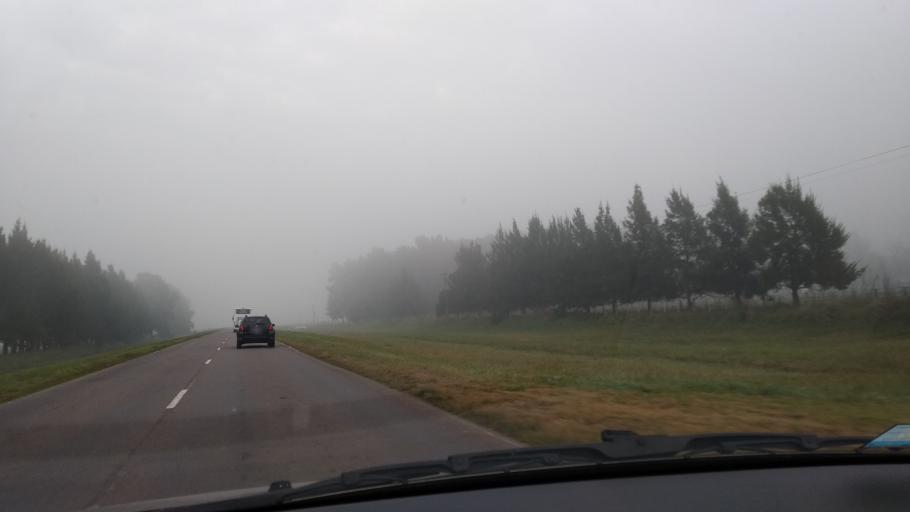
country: AR
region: Buenos Aires
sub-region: Partido de San Vicente
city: San Vicente
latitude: -35.2756
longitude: -58.5473
